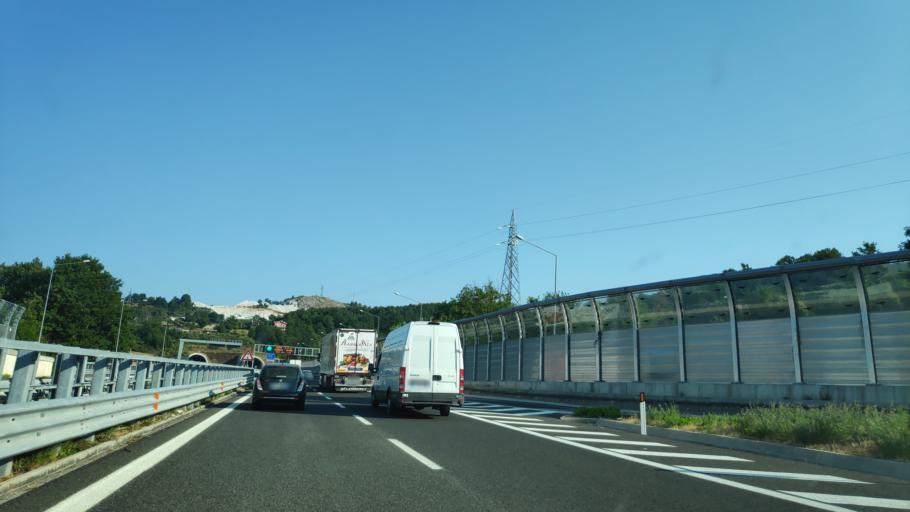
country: IT
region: Basilicate
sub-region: Provincia di Potenza
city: Lagonegro
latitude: 40.1357
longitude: 15.7602
